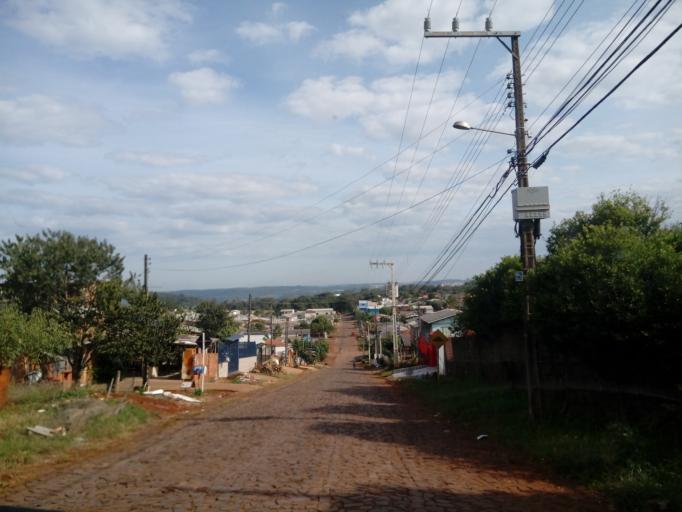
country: BR
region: Santa Catarina
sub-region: Chapeco
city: Chapeco
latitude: -27.1214
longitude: -52.6271
